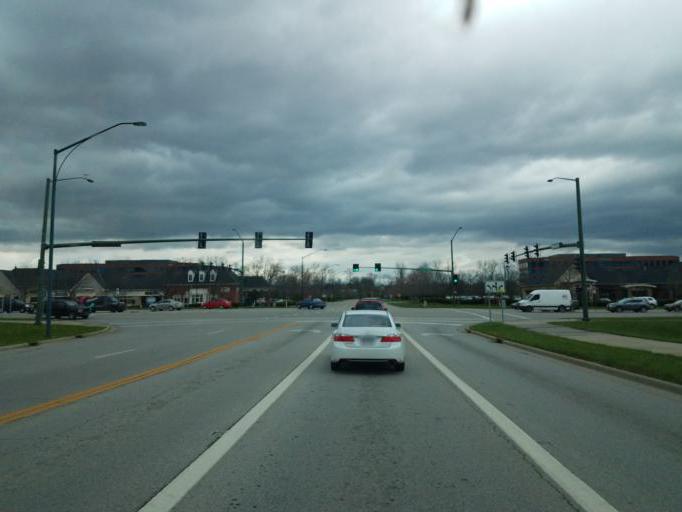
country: US
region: Ohio
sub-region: Franklin County
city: Westerville
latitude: 40.1451
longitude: -82.9466
